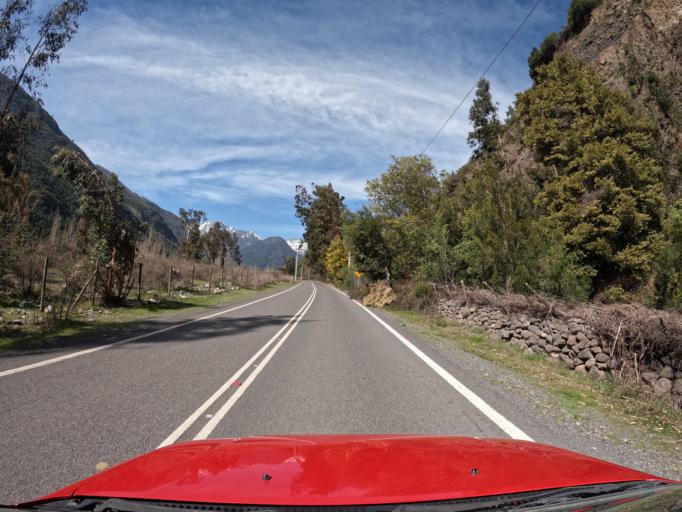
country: CL
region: O'Higgins
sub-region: Provincia de Colchagua
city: Chimbarongo
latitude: -35.0006
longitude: -70.8044
